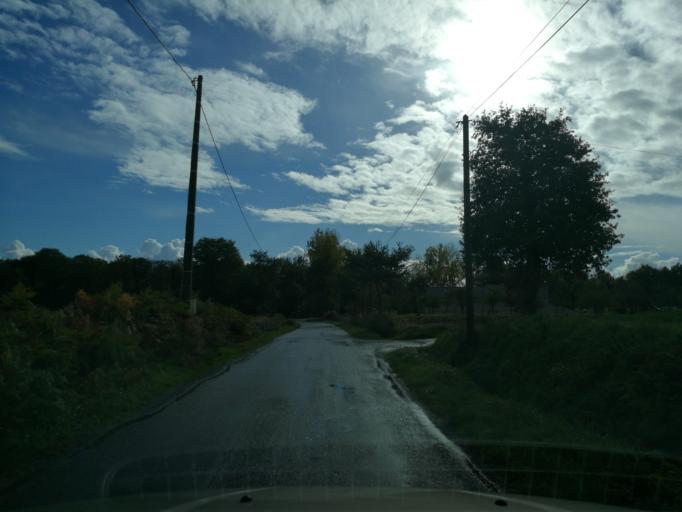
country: FR
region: Brittany
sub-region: Departement d'Ille-et-Vilaine
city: Pleumeleuc
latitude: 48.2054
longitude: -1.9326
